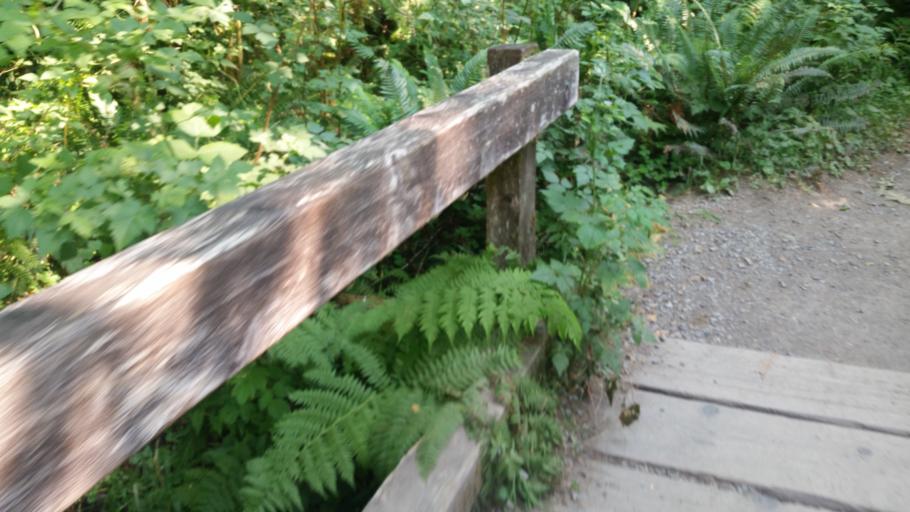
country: US
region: Washington
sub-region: Clallam County
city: Forks
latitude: 47.8611
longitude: -123.9335
